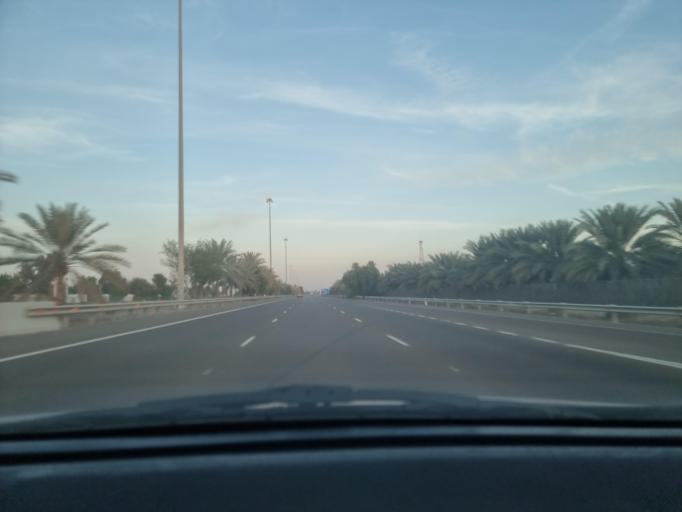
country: AE
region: Abu Dhabi
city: Al Ain
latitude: 24.1706
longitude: 55.1045
